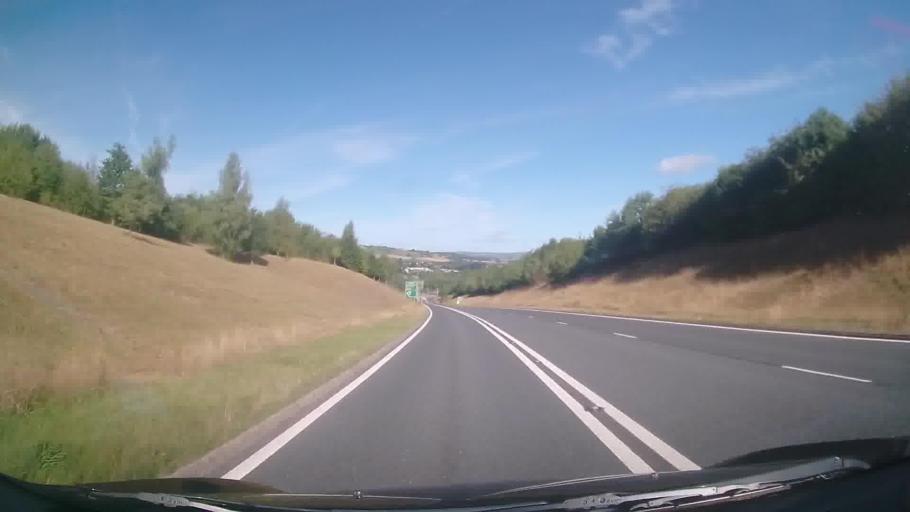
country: GB
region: Wales
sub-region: Sir Powys
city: Hay
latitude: 51.9906
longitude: -3.2336
